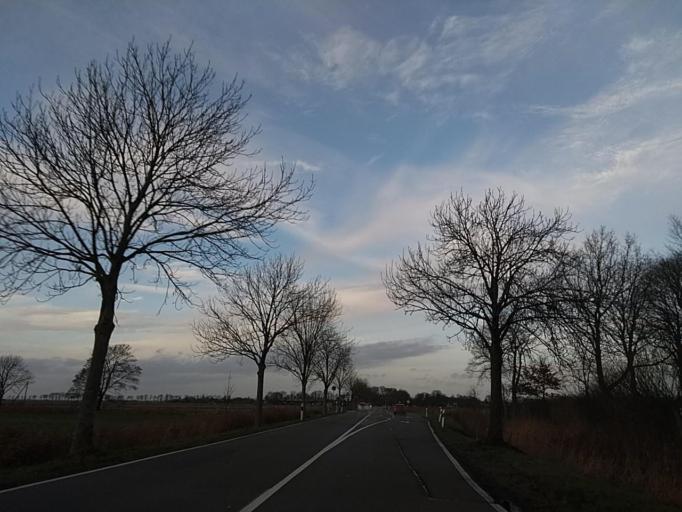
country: DE
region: Lower Saxony
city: Jemgum
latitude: 53.2554
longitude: 7.3859
